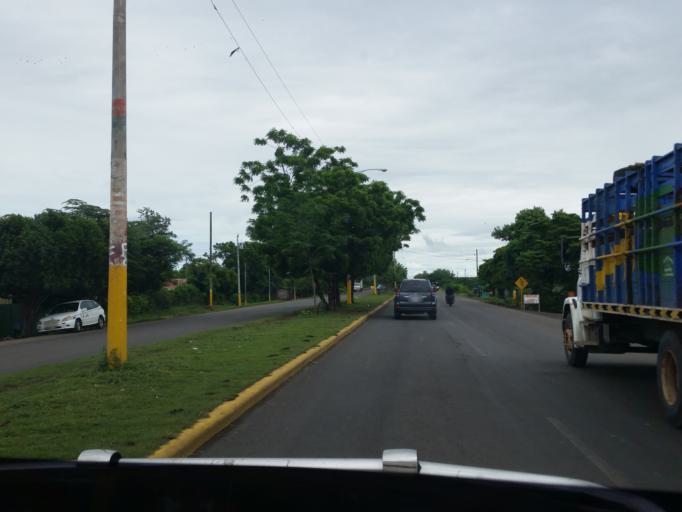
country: NI
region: Managua
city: Tipitapa
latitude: 12.1994
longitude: -86.1031
